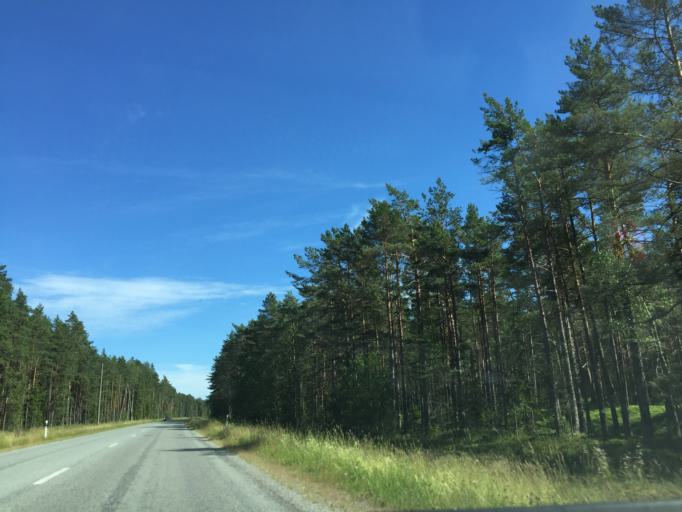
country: LV
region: Rojas
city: Roja
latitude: 57.4920
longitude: 22.8319
